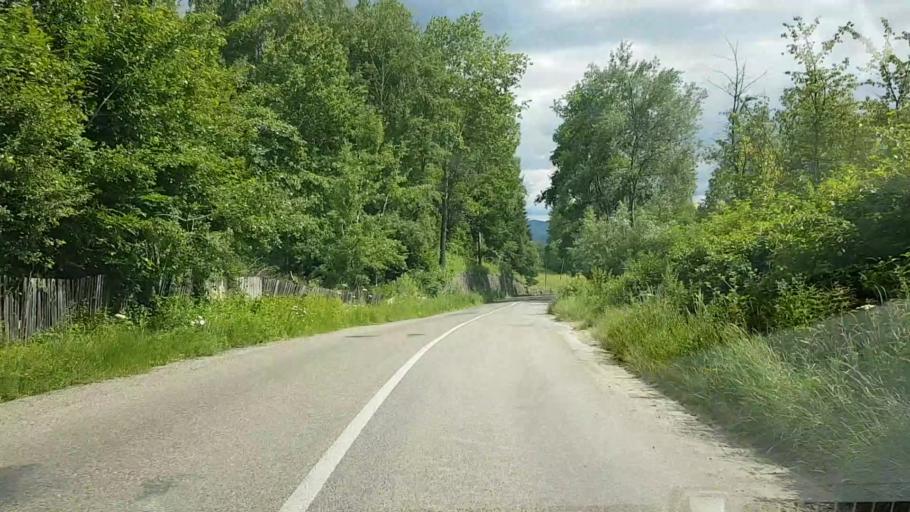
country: RO
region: Neamt
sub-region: Comuna Ceahlau
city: Ceahlau
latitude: 47.0655
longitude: 25.9622
